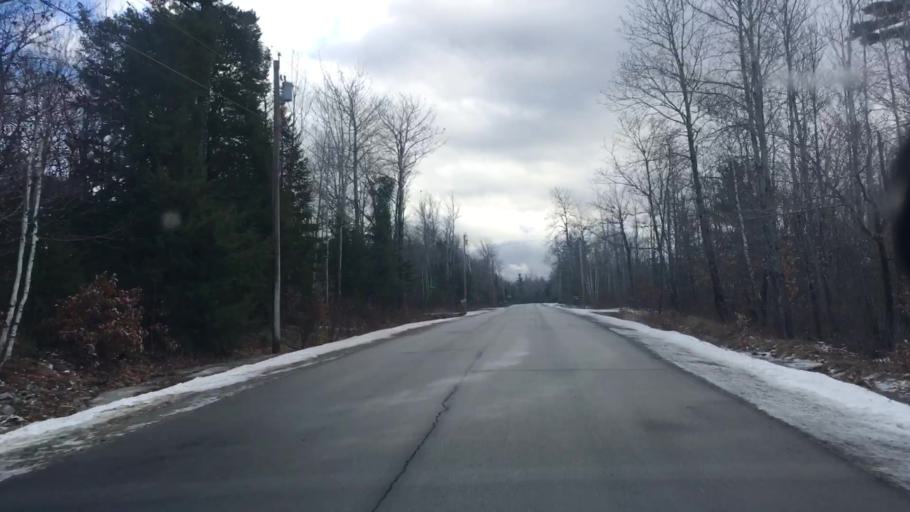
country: US
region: Maine
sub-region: Hancock County
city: Dedham
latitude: 44.6833
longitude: -68.7089
